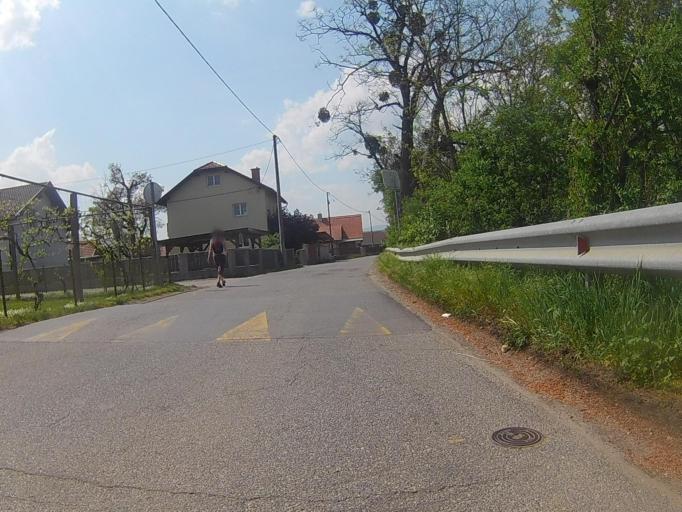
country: SI
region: Maribor
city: Maribor
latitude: 46.5508
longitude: 15.6866
